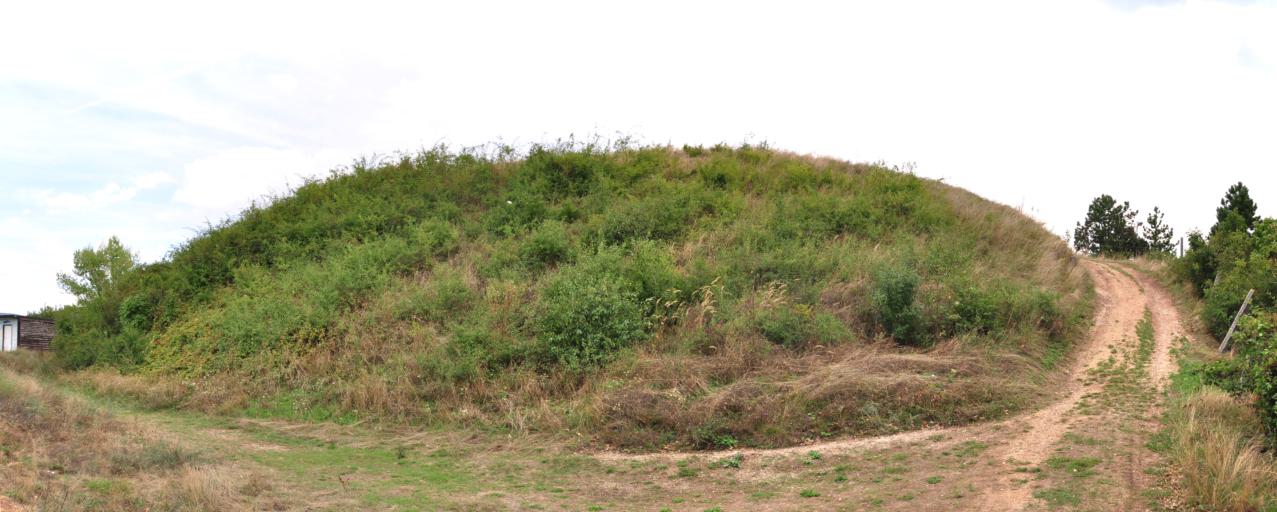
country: SK
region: Trnavsky
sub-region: Okres Trnava
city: Piestany
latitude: 48.6230
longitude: 17.8727
